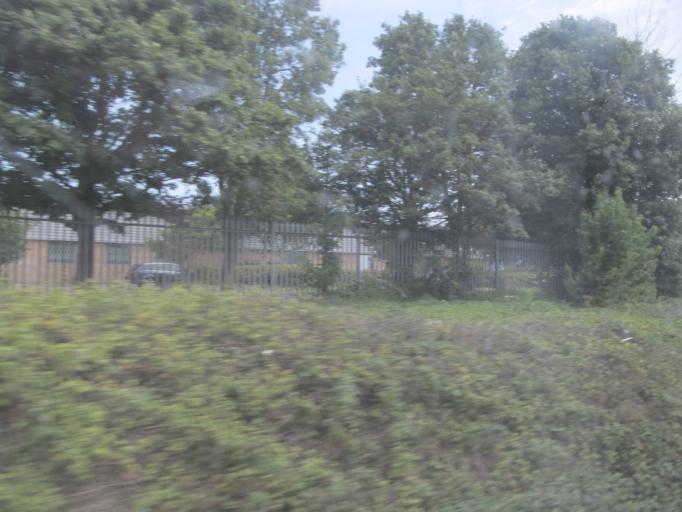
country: GB
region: England
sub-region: Buckinghamshire
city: Farnham Royal
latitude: 51.5197
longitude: -0.6240
